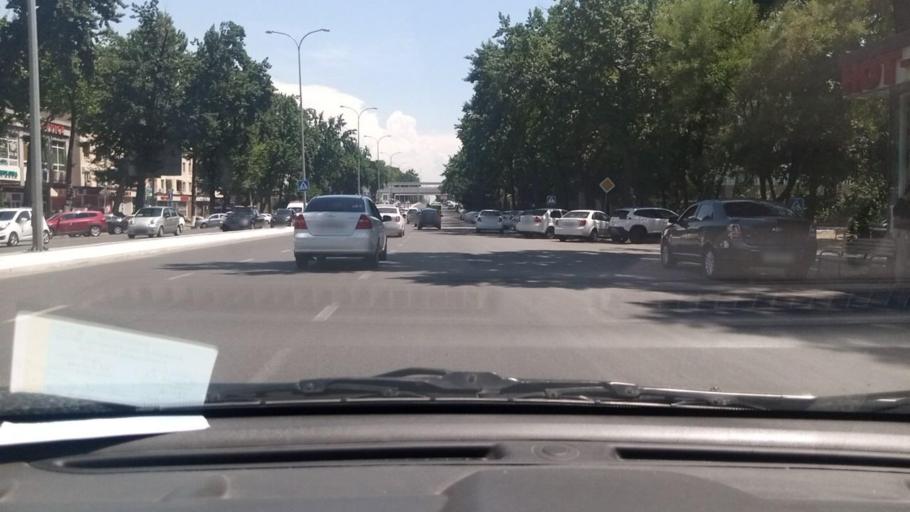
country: UZ
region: Toshkent Shahri
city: Tashkent
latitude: 41.2846
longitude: 69.2085
